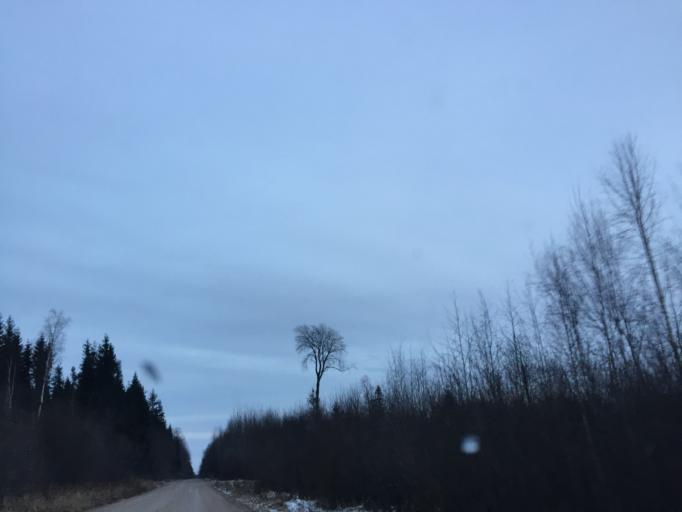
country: LV
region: Burtnieki
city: Matisi
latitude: 57.6324
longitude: 25.1230
